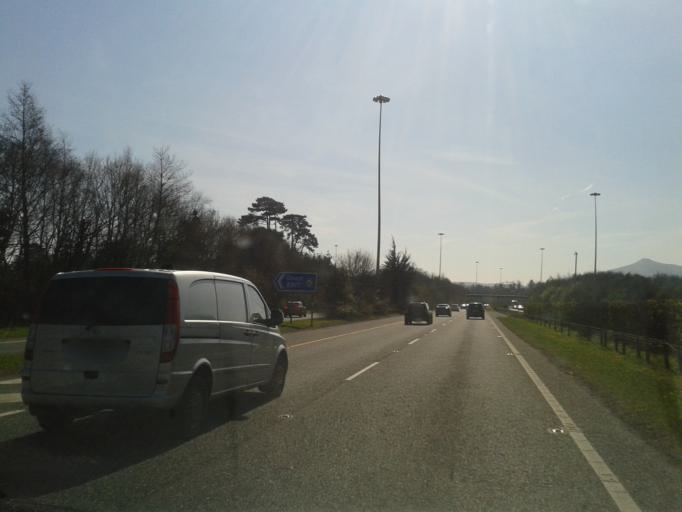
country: IE
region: Leinster
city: Shankill
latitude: 53.2165
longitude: -6.1266
